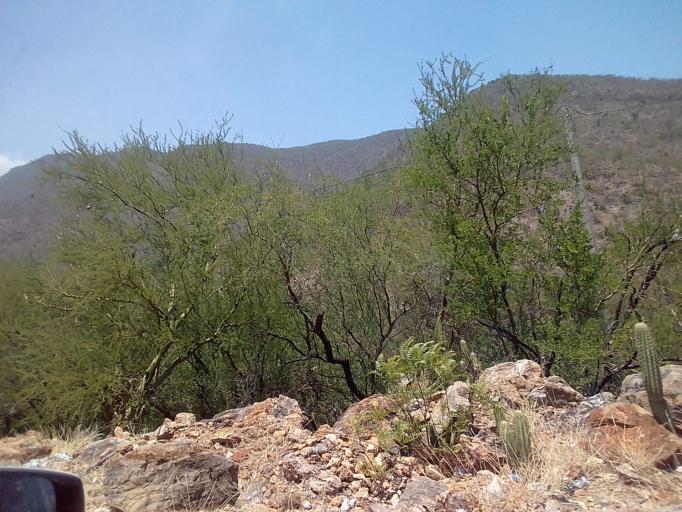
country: MX
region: Oaxaca
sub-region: San Pedro Quiatoni
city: San Pedro Quiatoni
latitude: 16.6725
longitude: -96.1448
